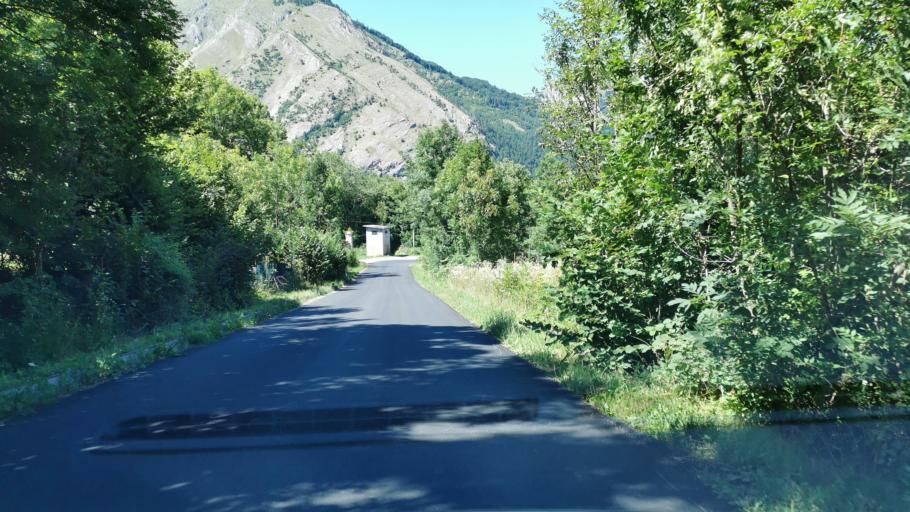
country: IT
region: Piedmont
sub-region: Provincia di Cuneo
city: Entracque
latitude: 44.2523
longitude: 7.3835
